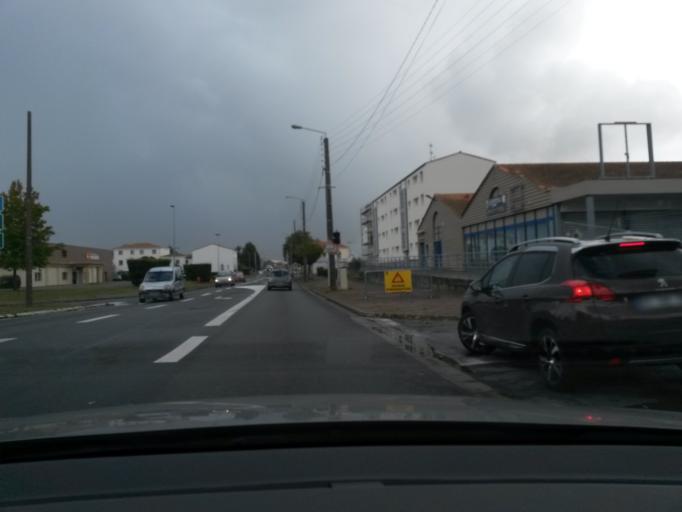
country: FR
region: Poitou-Charentes
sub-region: Departement de la Charente-Maritime
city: Rochefort
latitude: 45.9454
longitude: -0.9561
